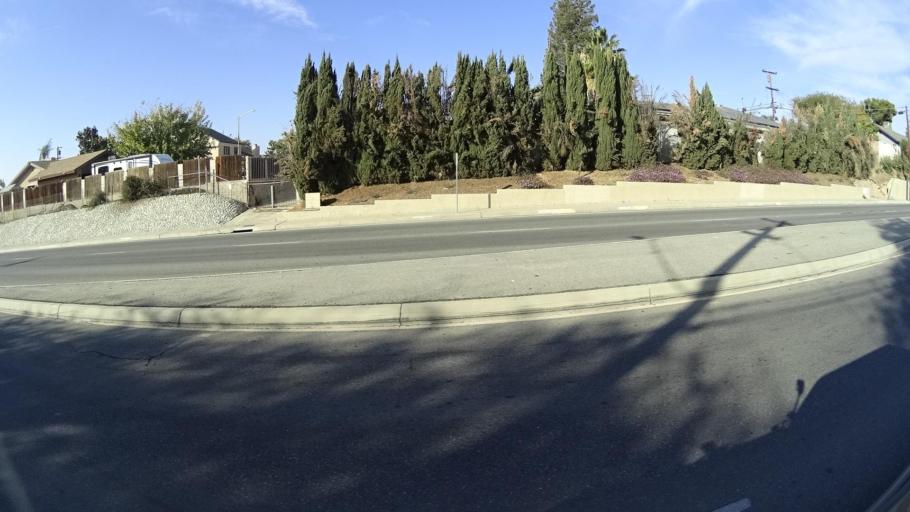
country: US
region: California
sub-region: Kern County
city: Bakersfield
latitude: 35.3852
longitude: -118.9503
